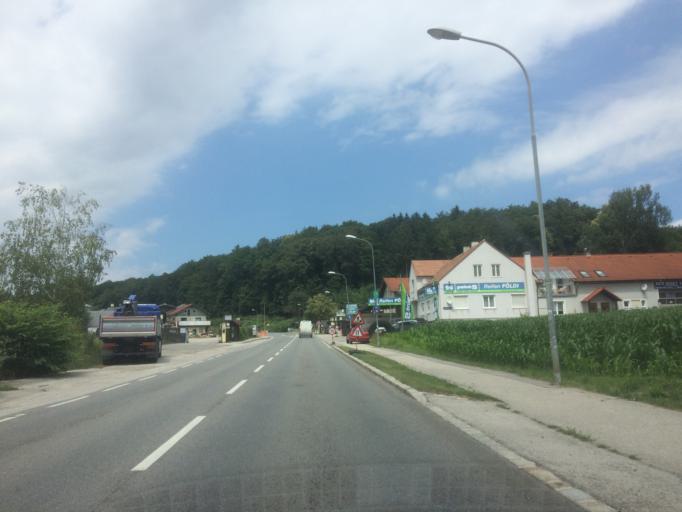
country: AT
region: Lower Austria
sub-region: Politischer Bezirk Wien-Umgebung
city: Gablitz
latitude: 48.2400
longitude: 16.1356
